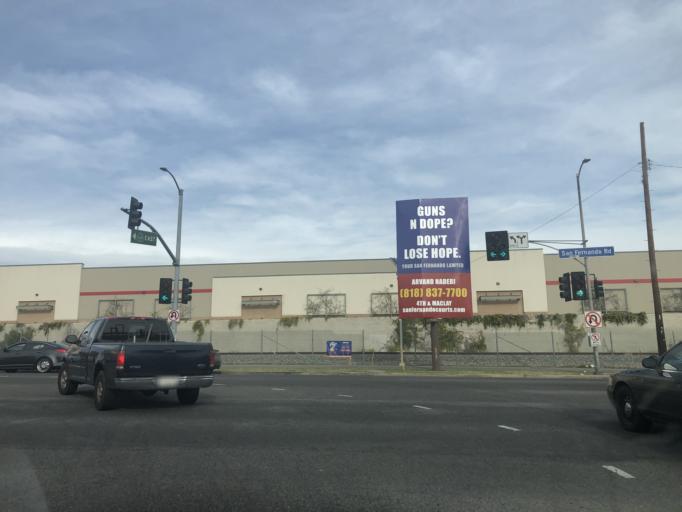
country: US
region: California
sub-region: Los Angeles County
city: San Fernando
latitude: 34.2712
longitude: -118.4276
